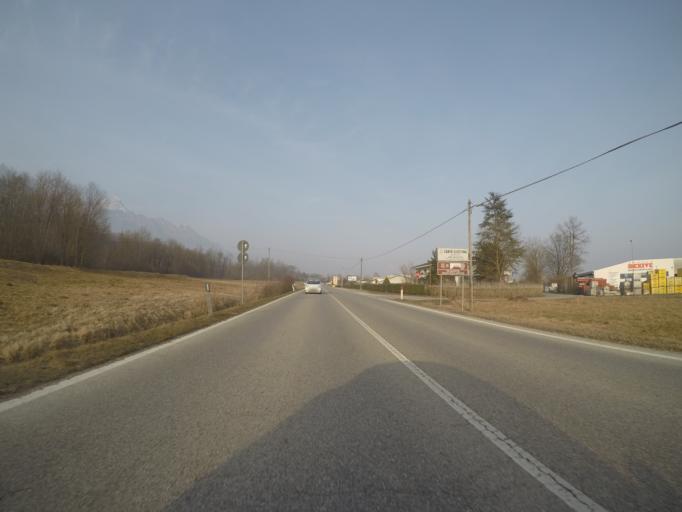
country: IT
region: Veneto
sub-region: Provincia di Belluno
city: Santa Giustina
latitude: 46.0704
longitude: 12.0169
